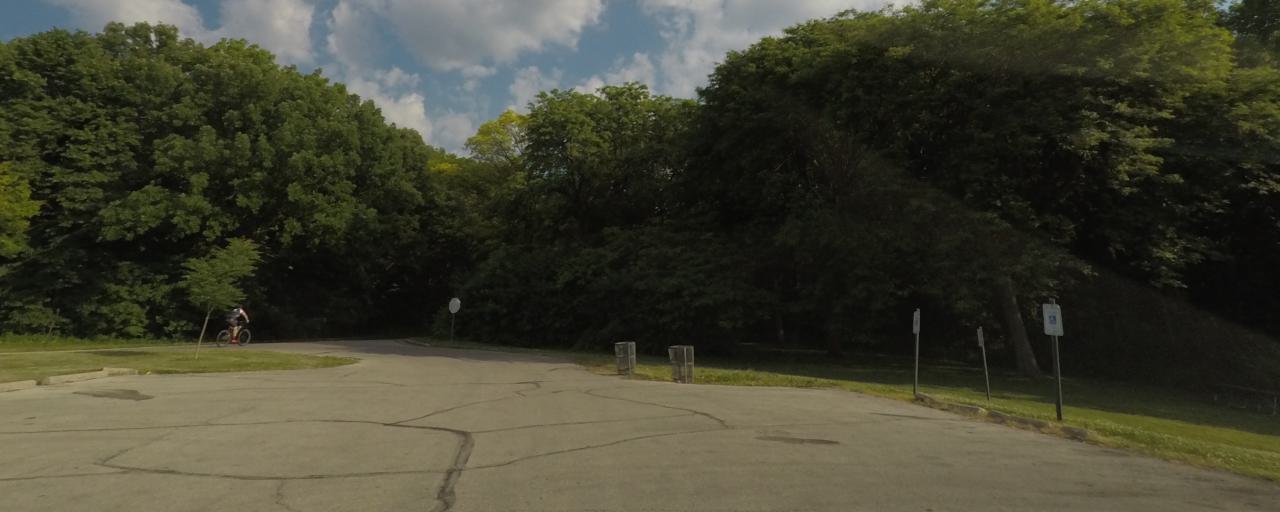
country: US
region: Wisconsin
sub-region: Milwaukee County
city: Hales Corners
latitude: 42.9263
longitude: -88.0298
